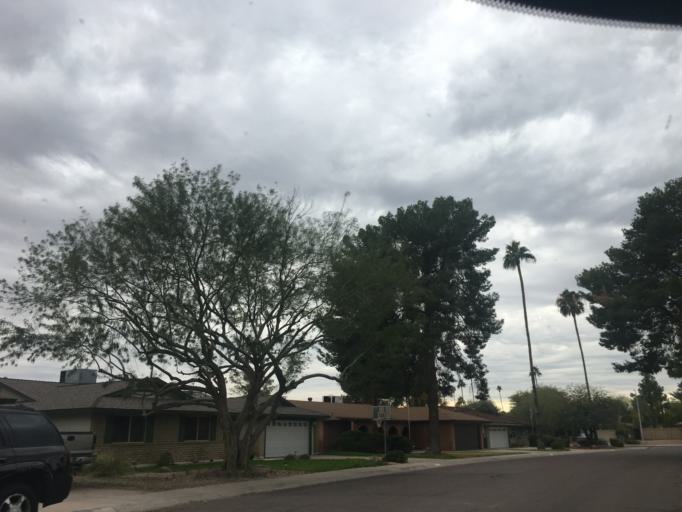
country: US
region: Arizona
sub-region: Maricopa County
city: Guadalupe
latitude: 33.3699
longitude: -111.9256
